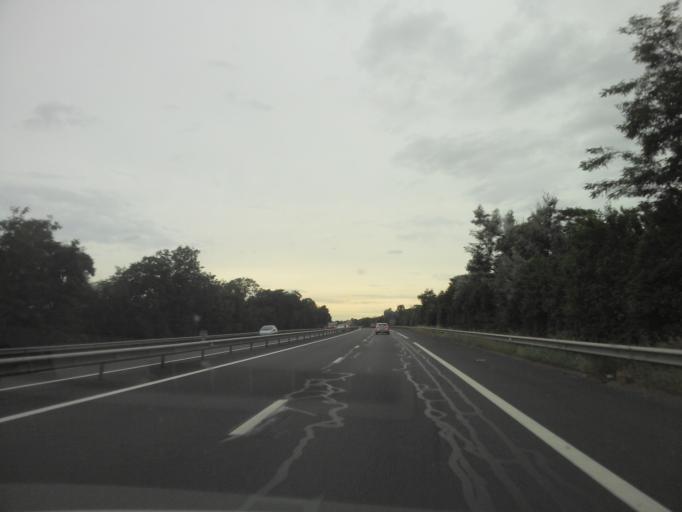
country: FR
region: Auvergne
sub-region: Departement du Puy-de-Dome
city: Riom
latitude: 45.9143
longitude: 3.1517
